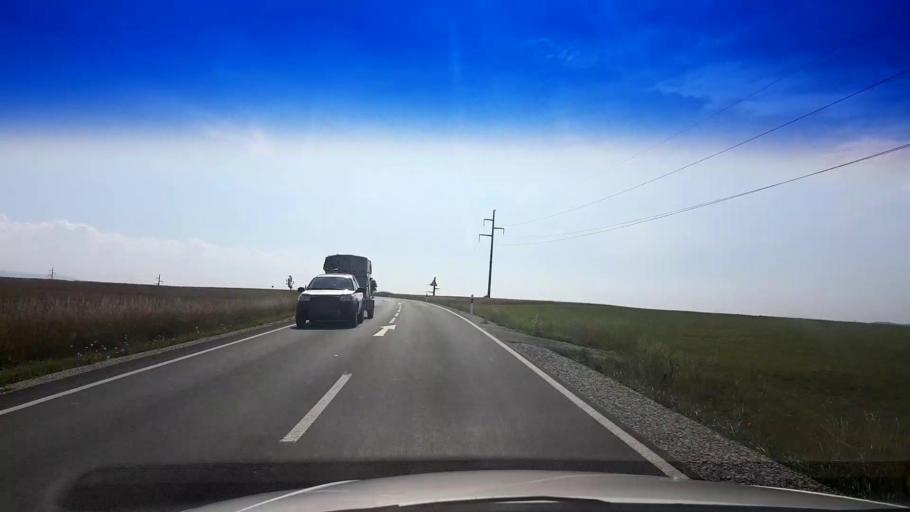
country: DE
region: Bavaria
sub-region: Upper Franconia
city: Mistelgau
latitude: 49.9361
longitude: 11.4680
